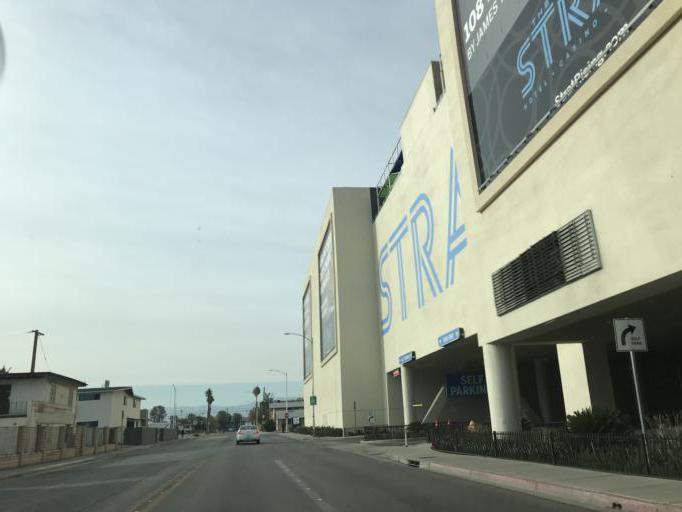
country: US
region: Nevada
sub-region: Clark County
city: Las Vegas
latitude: 36.1464
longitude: -115.1569
